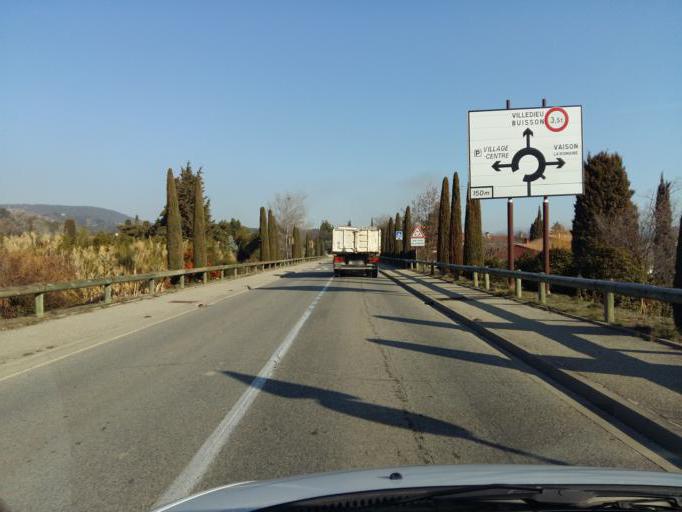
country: FR
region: Provence-Alpes-Cote d'Azur
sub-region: Departement du Vaucluse
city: Sablet
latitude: 44.2434
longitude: 5.0173
